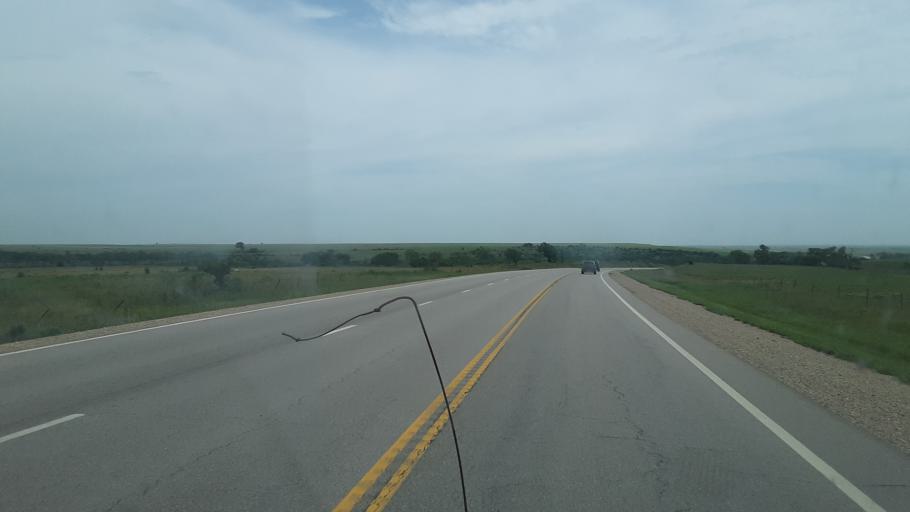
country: US
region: Kansas
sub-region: Greenwood County
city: Eureka
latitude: 37.8152
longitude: -96.4774
